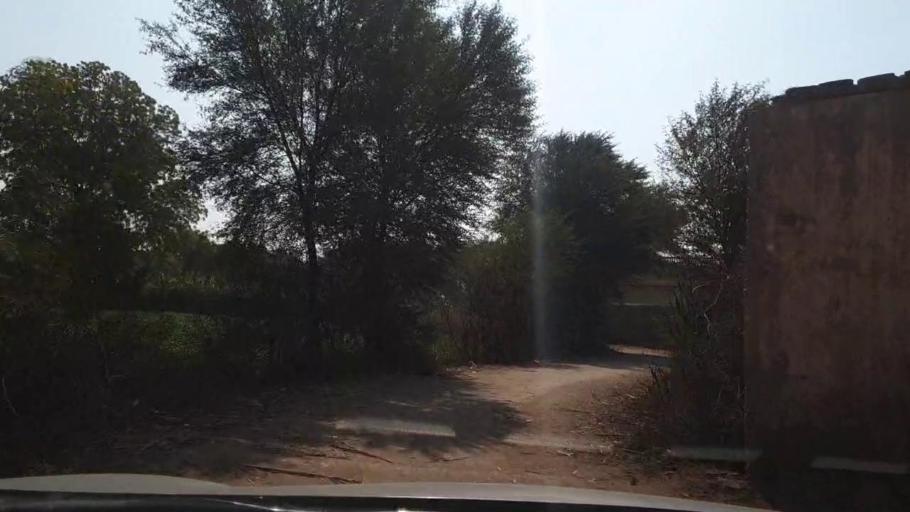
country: PK
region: Sindh
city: Tando Allahyar
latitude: 25.5328
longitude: 68.7684
